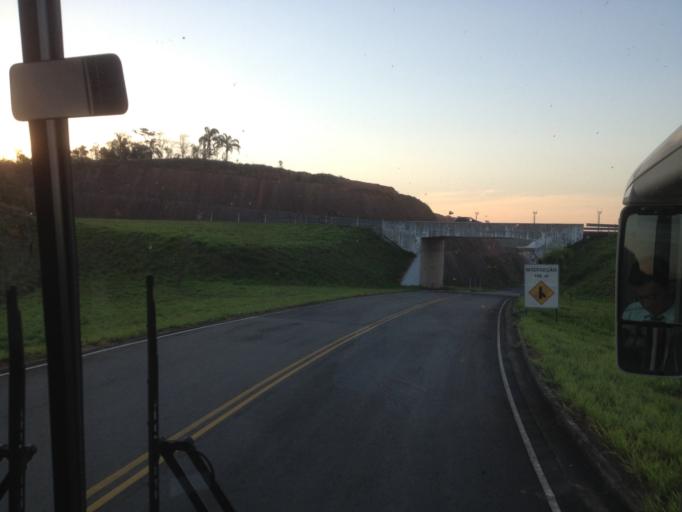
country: BR
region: Minas Gerais
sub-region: Rio Novo
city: Rio Novo
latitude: -21.5128
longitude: -43.1598
